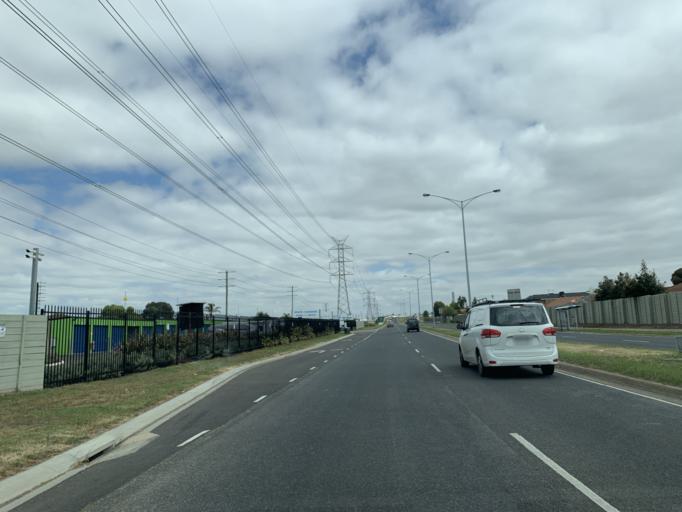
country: AU
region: Victoria
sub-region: Moonee Valley
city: Keilor East
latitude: -37.7407
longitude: 144.8598
